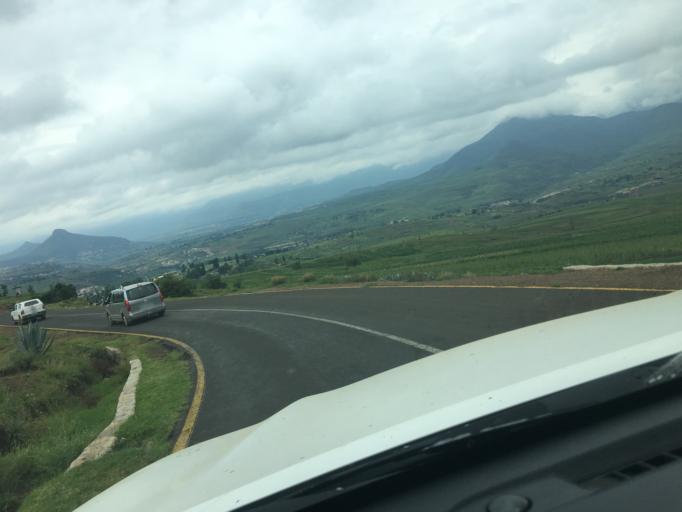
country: LS
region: Berea
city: Teyateyaneng
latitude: -29.2564
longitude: 27.8427
